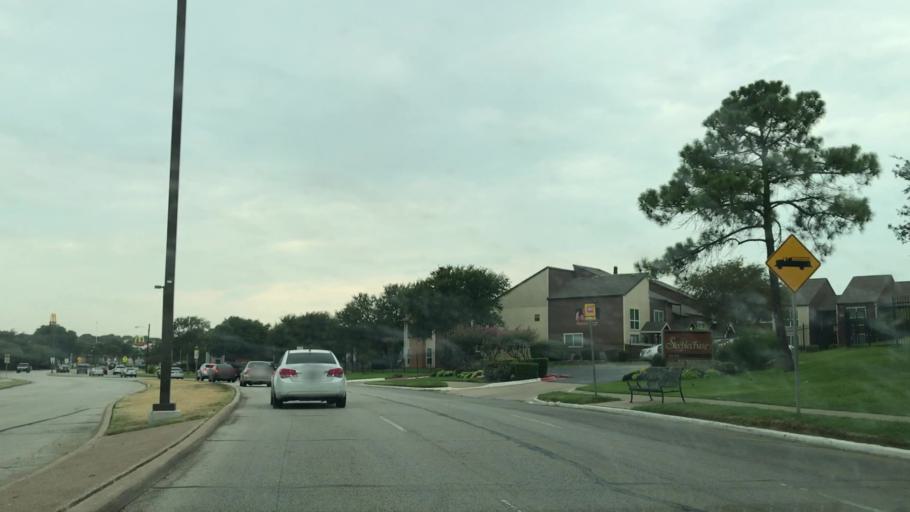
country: US
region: Texas
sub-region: Dallas County
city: Irving
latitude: 32.8662
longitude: -96.9869
